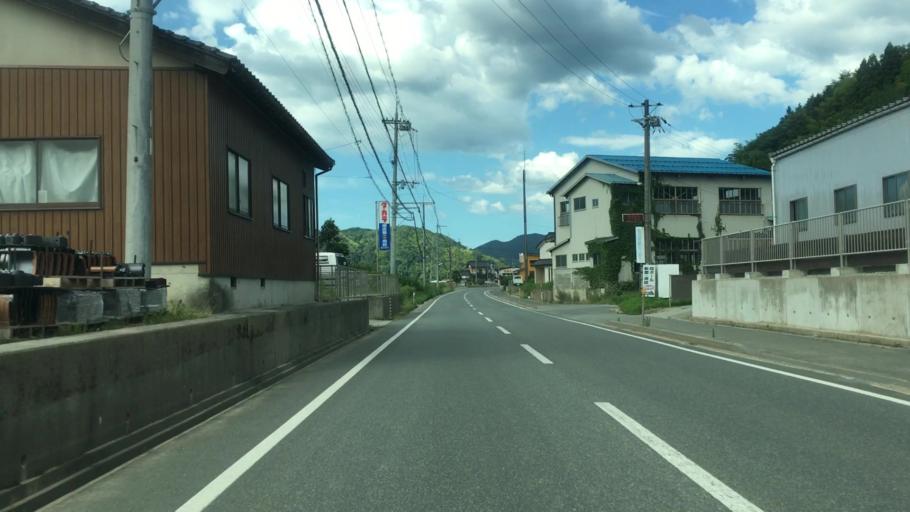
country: JP
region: Hyogo
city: Toyooka
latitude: 35.5537
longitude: 134.7933
